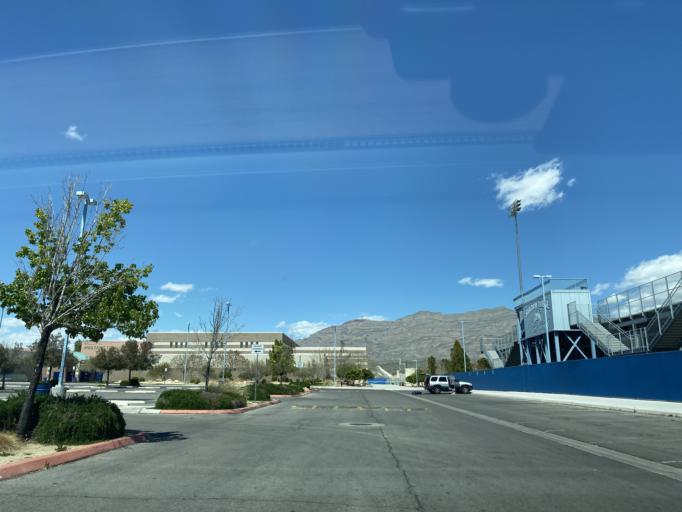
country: US
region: Nevada
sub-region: Clark County
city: North Las Vegas
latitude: 36.3174
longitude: -115.2092
